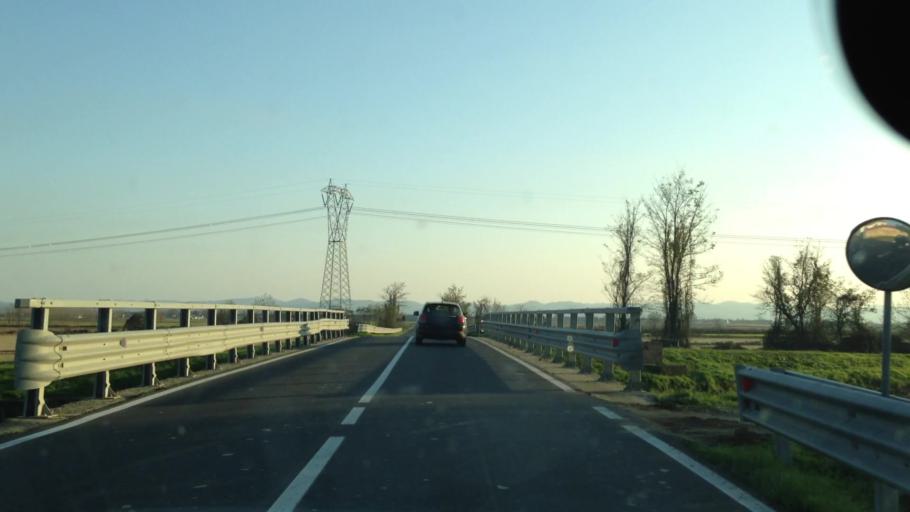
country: IT
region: Piedmont
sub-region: Provincia di Vercelli
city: Lamporo
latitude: 45.2458
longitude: 8.0902
